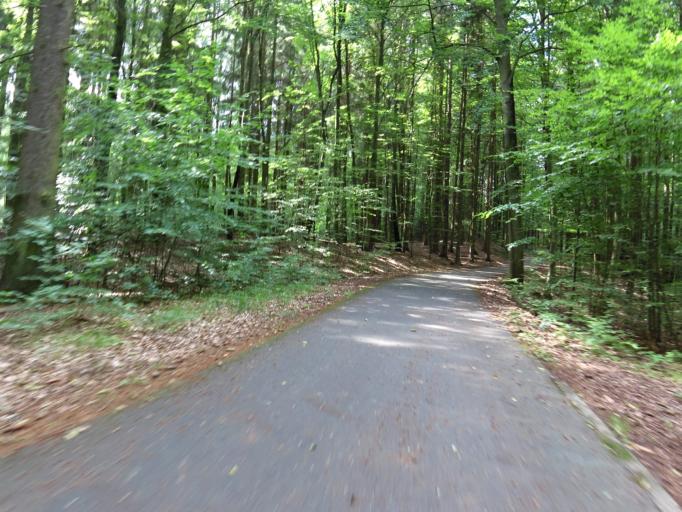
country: DE
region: Brandenburg
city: Lychen
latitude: 53.1873
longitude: 13.3445
